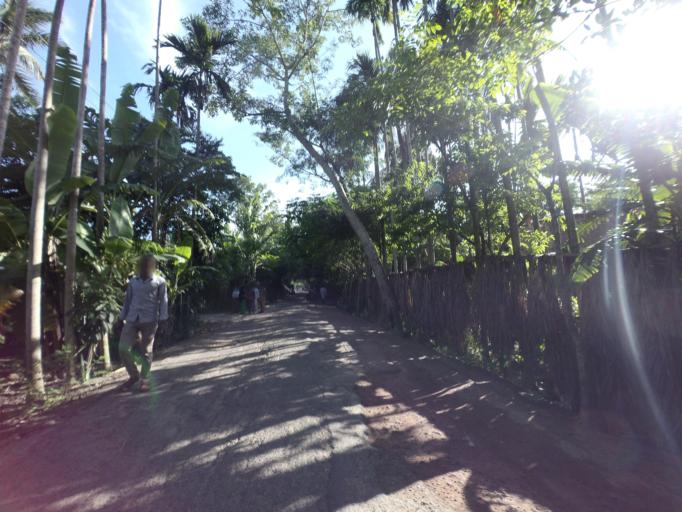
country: BD
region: Khulna
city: Kalia
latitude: 23.0082
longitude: 89.5837
